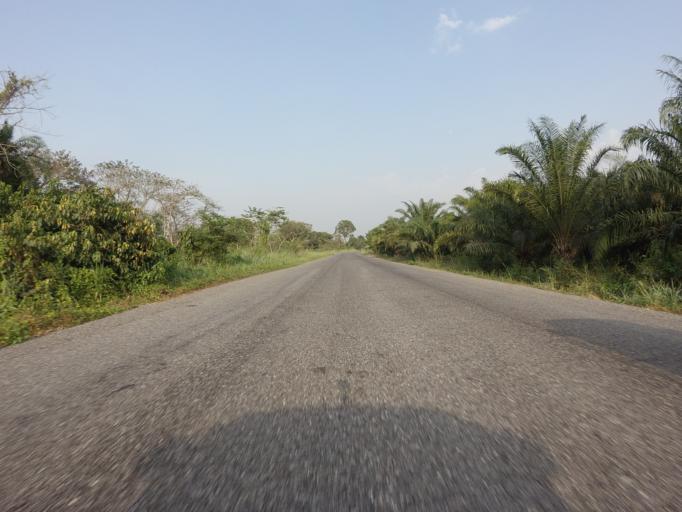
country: GH
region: Volta
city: Ho
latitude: 6.4384
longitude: 0.1964
